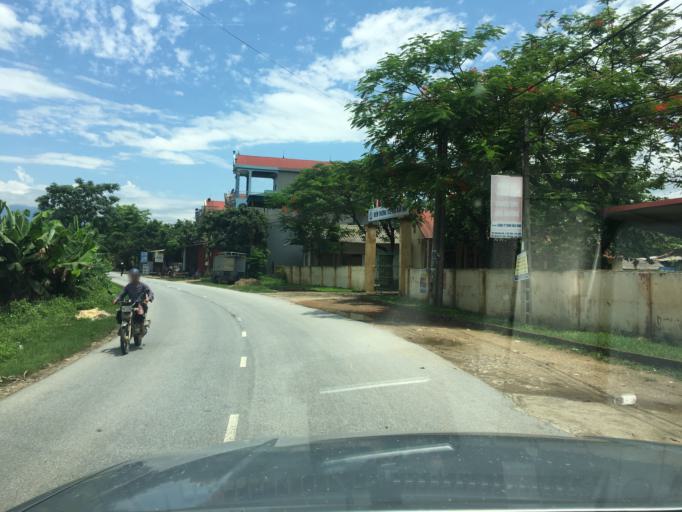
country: VN
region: Yen Bai
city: Son Thinh
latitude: 21.6440
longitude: 104.5004
